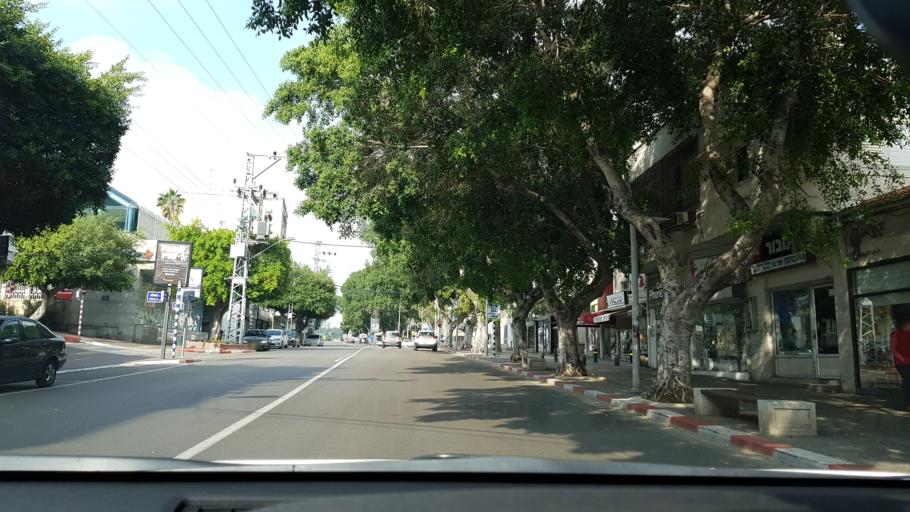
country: IL
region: Central District
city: Ness Ziona
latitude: 31.8980
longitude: 34.8105
